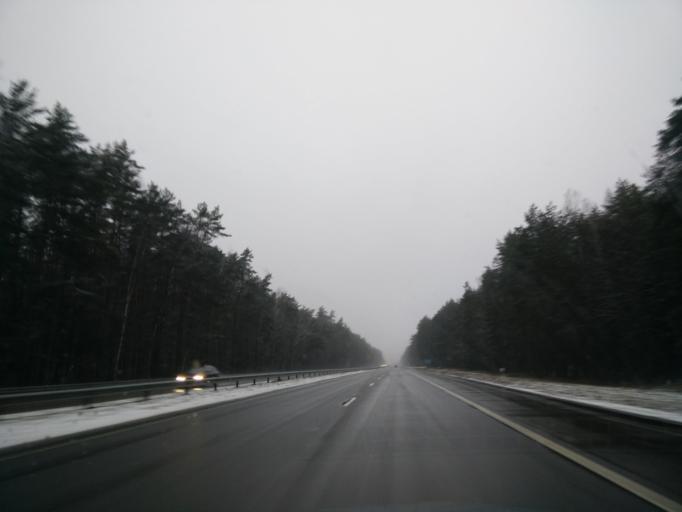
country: LT
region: Vilnius County
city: Lazdynai
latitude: 54.6444
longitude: 25.1754
